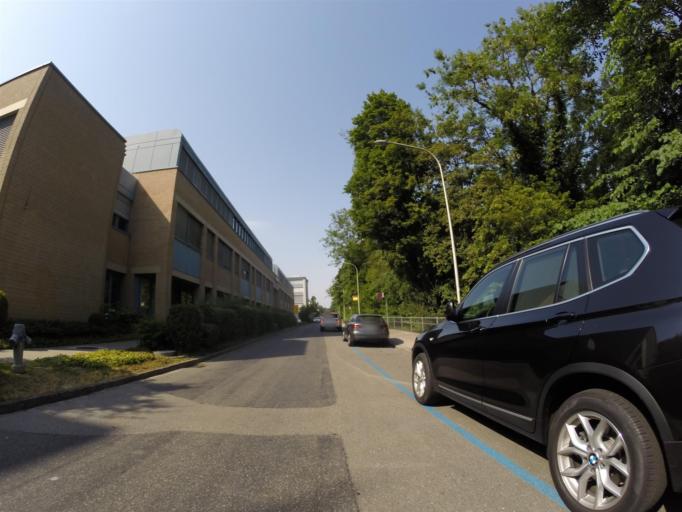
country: CH
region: Bern
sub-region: Bern-Mittelland District
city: Bern
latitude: 46.9571
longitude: 7.4403
